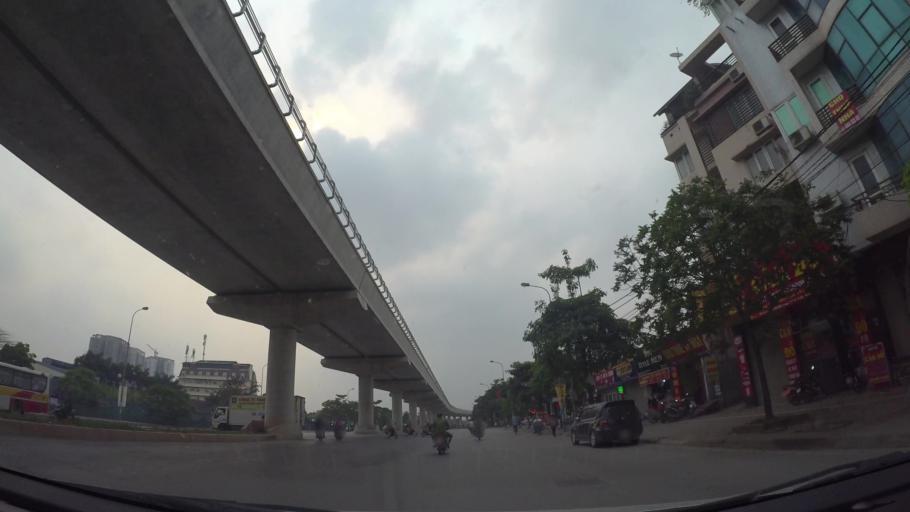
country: VN
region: Ha Noi
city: Cau Dien
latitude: 21.0498
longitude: 105.7405
